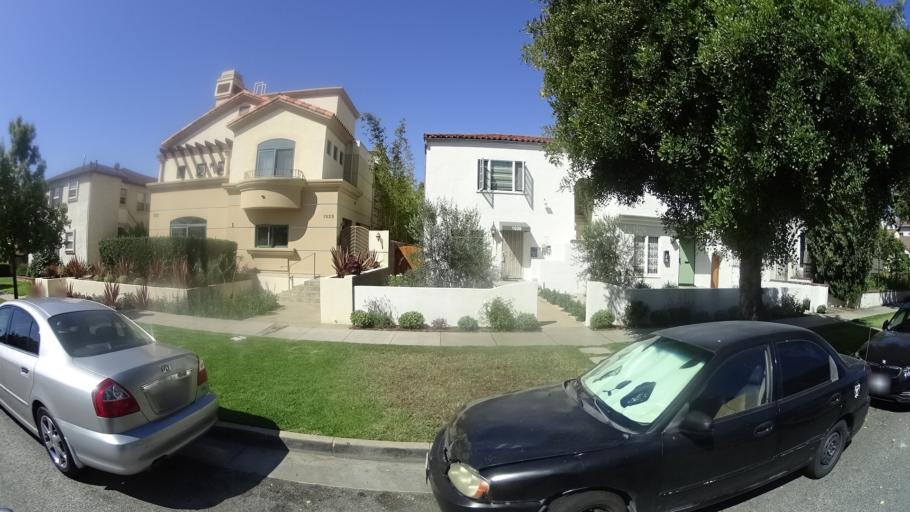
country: US
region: California
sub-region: Los Angeles County
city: Santa Monica
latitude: 34.0260
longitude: -118.4953
